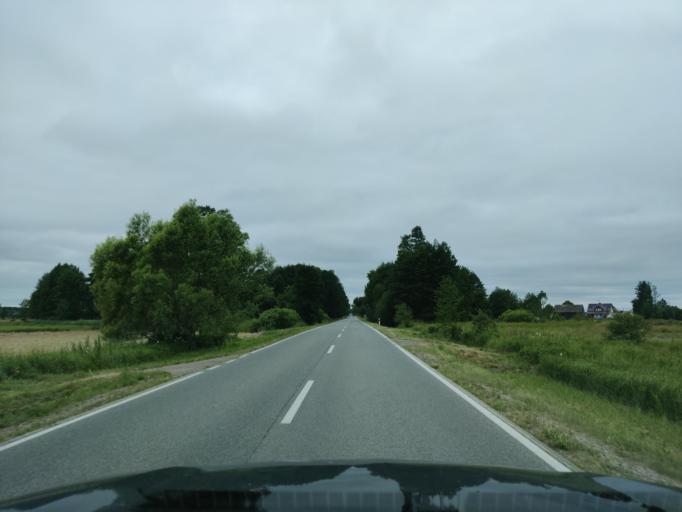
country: PL
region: Masovian Voivodeship
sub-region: Powiat ostrolecki
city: Czarnia
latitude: 53.3250
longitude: 21.1596
